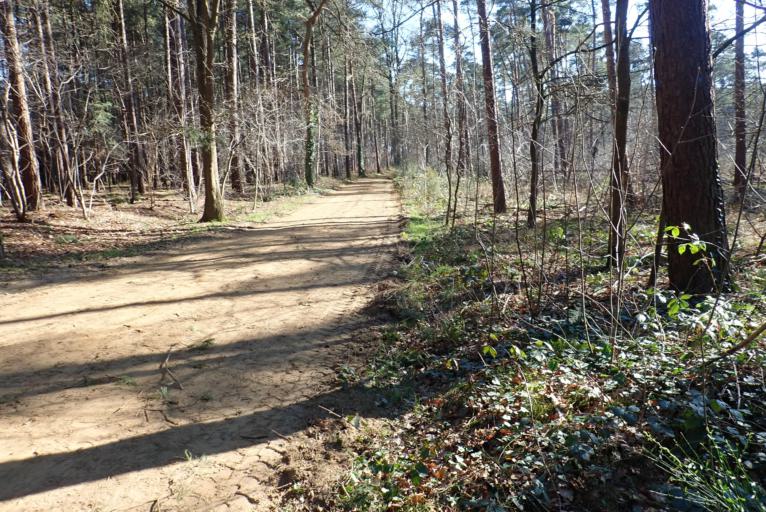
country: BE
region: Flanders
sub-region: Provincie Antwerpen
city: Lille
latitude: 51.2509
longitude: 4.8678
